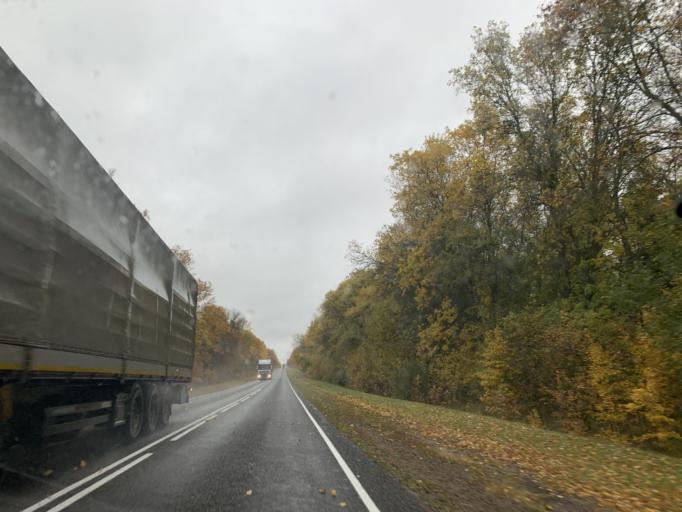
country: BY
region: Minsk
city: Novy Svyerzhan'
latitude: 53.4409
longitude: 26.6581
